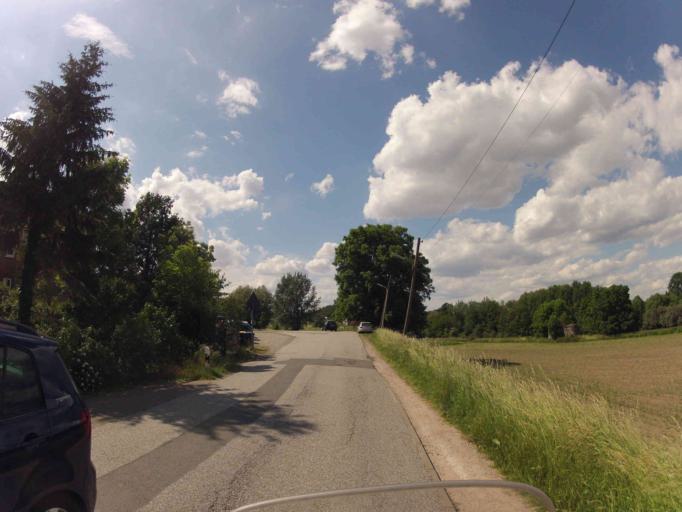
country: DE
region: Hamburg
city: Rothenburgsort
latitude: 53.4972
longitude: 10.0806
